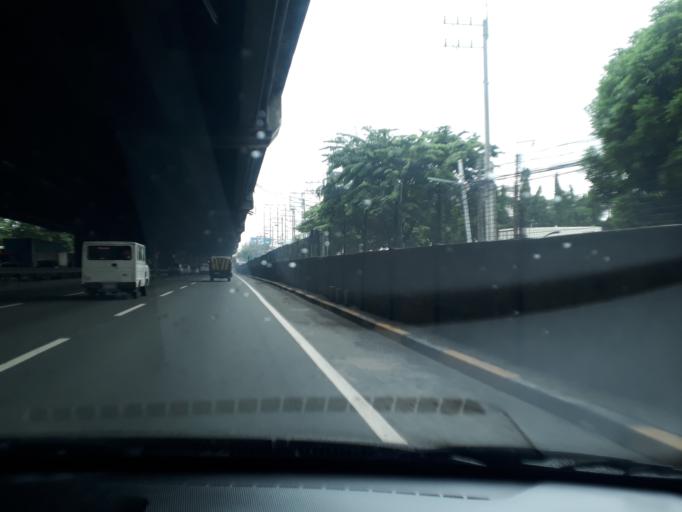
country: PH
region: Calabarzon
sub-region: Province of Rizal
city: Taguig
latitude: 14.5027
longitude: 121.0371
